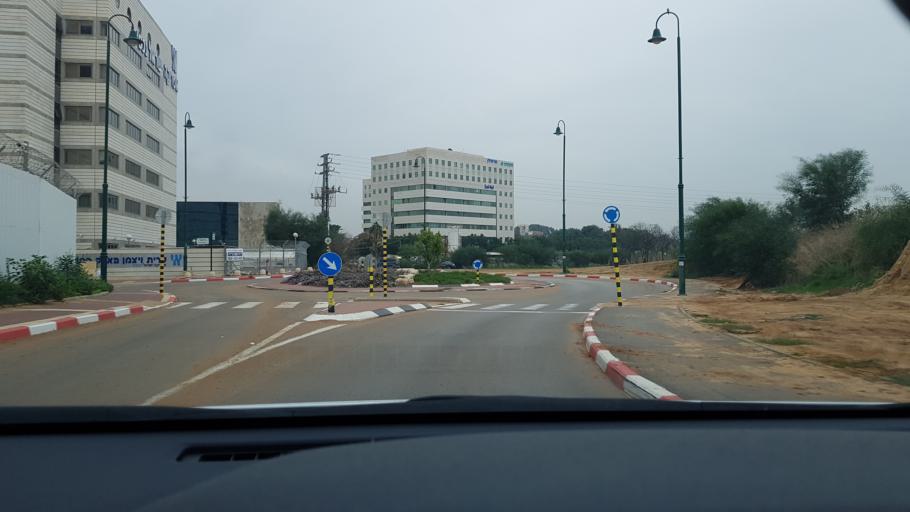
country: IL
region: Central District
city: Ness Ziona
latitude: 31.9169
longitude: 34.8035
